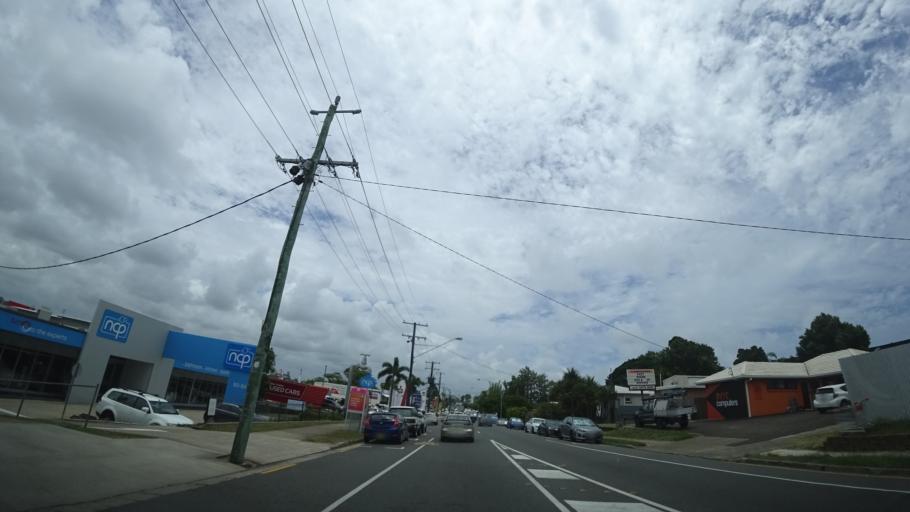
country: AU
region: Queensland
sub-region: Sunshine Coast
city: Mooloolaba
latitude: -26.6692
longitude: 153.0949
